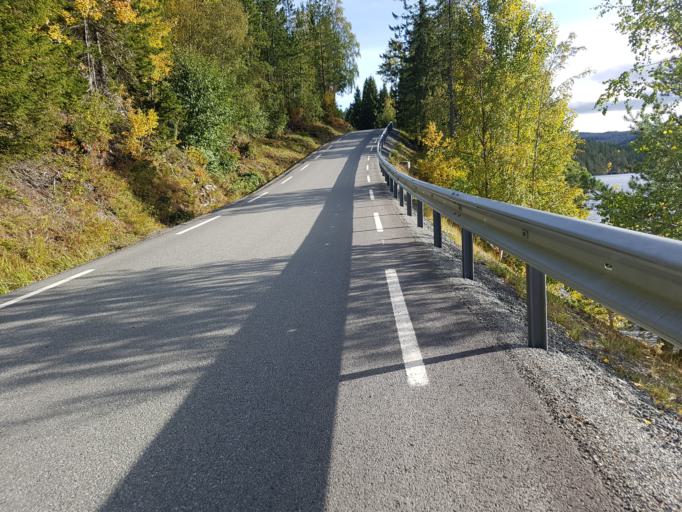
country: NO
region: Sor-Trondelag
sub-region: Malvik
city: Malvik
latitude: 63.3587
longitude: 10.6344
